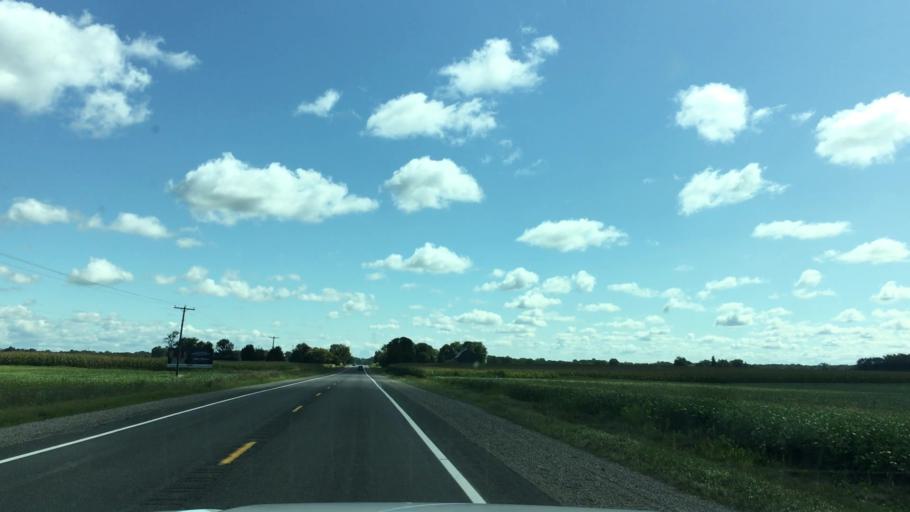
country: US
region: Michigan
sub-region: Montcalm County
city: Carson City
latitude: 43.1773
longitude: -84.8928
